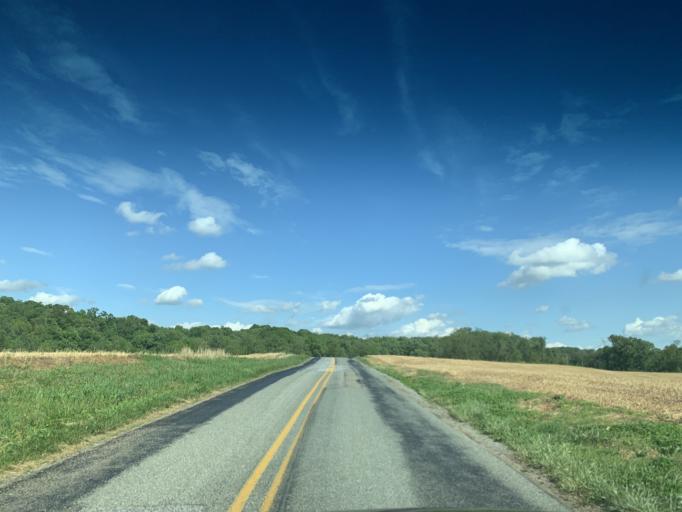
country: US
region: Maryland
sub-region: Cecil County
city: Rising Sun
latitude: 39.7232
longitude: -76.1809
